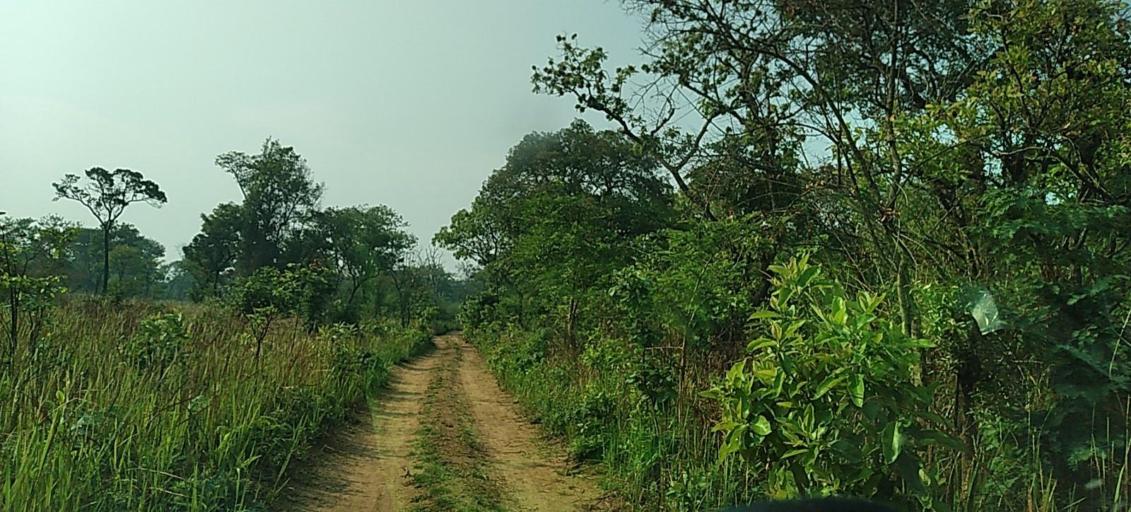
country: ZM
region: North-Western
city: Solwezi
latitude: -12.4007
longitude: 26.5854
